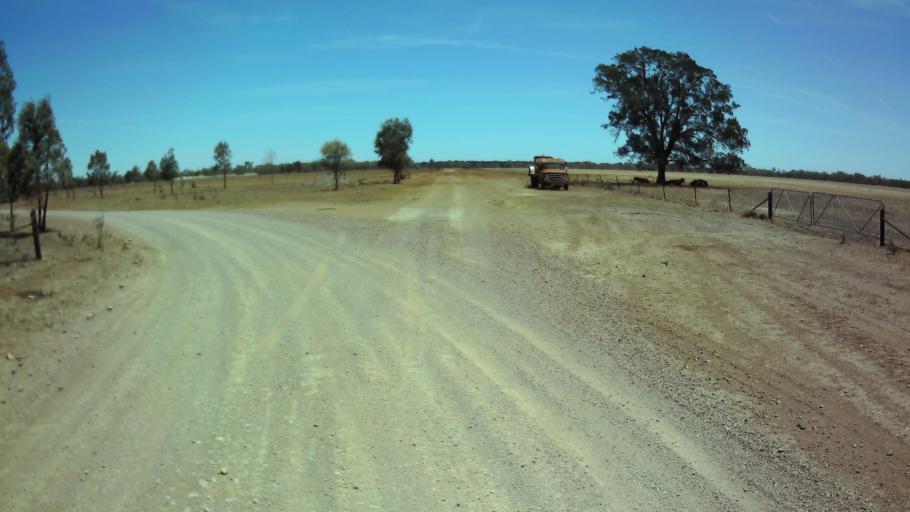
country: AU
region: New South Wales
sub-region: Bland
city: West Wyalong
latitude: -33.8234
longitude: 147.6425
